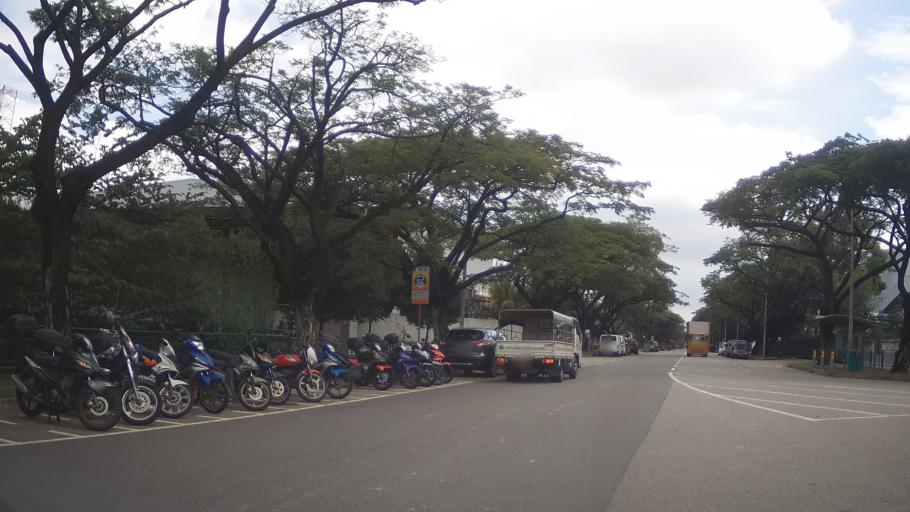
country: MY
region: Johor
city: Johor Bahru
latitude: 1.3077
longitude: 103.6495
